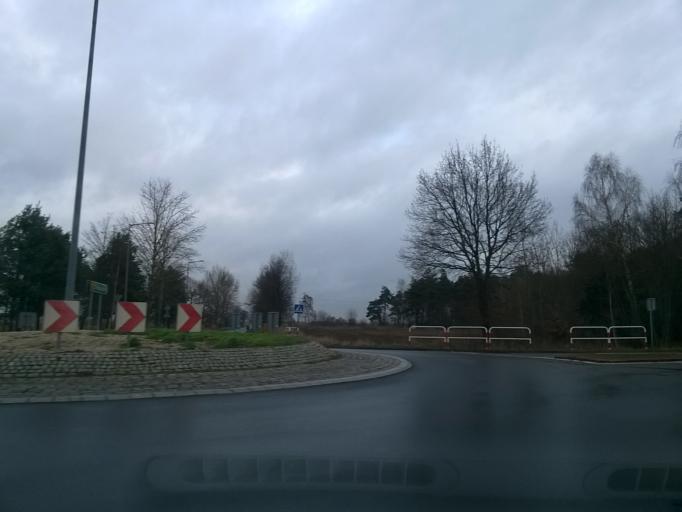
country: PL
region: Greater Poland Voivodeship
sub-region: Powiat wagrowiecki
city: Golancz
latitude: 52.9137
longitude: 17.3671
